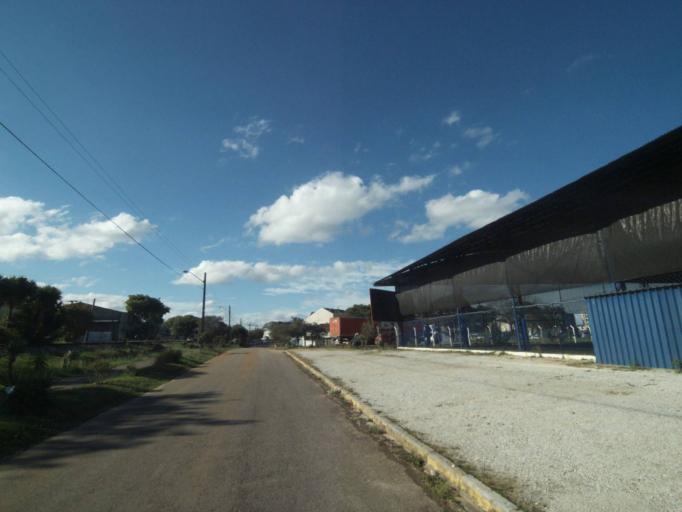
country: BR
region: Parana
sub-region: Curitiba
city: Curitiba
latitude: -25.3929
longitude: -49.2579
